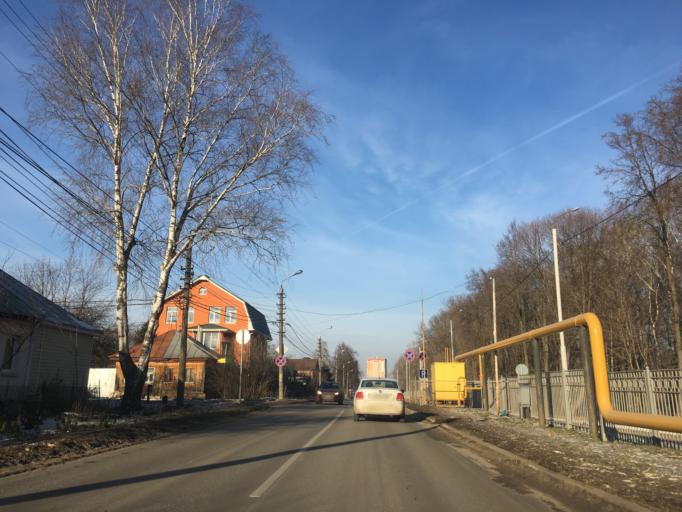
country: RU
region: Tula
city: Tula
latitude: 54.1809
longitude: 37.5771
